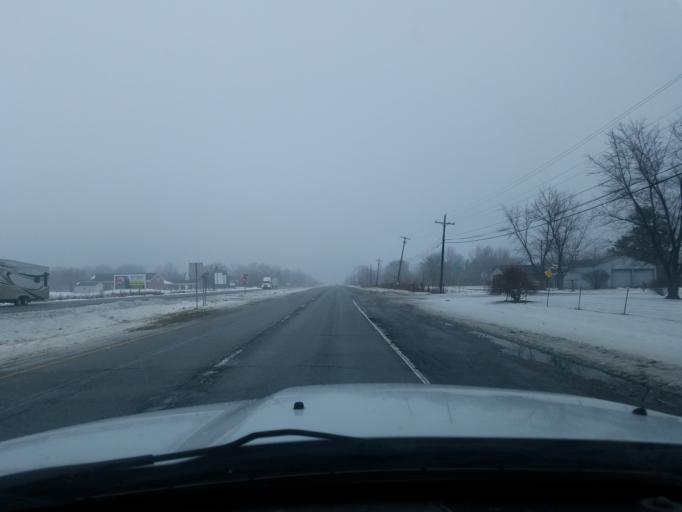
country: US
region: Indiana
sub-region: Howard County
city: Kokomo
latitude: 40.5532
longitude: -86.1270
